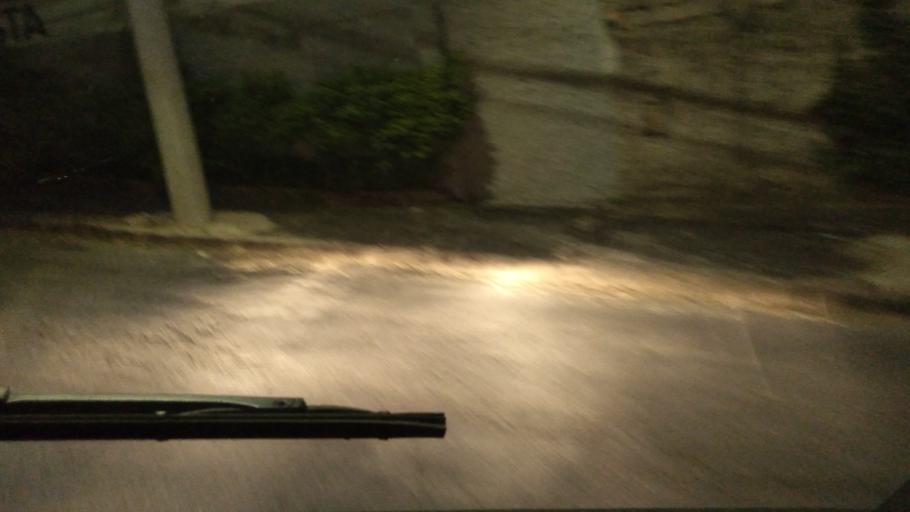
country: BR
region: Minas Gerais
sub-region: Belo Horizonte
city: Belo Horizonte
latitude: -19.8758
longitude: -43.9366
